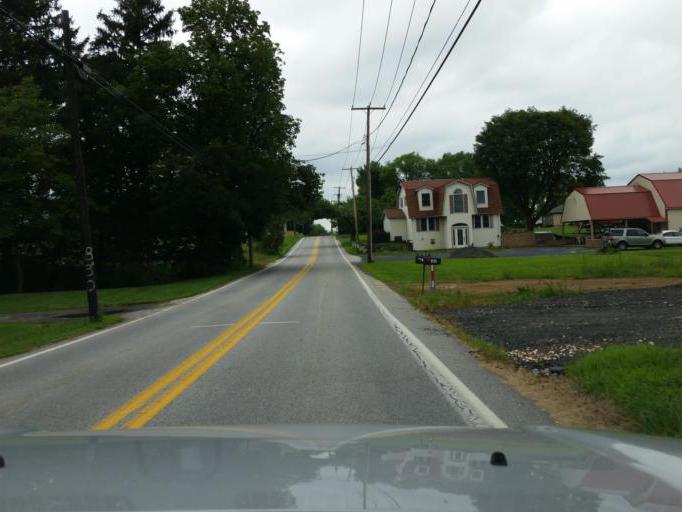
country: US
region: Pennsylvania
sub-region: Dauphin County
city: Rutherford
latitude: 40.2757
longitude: -76.7863
